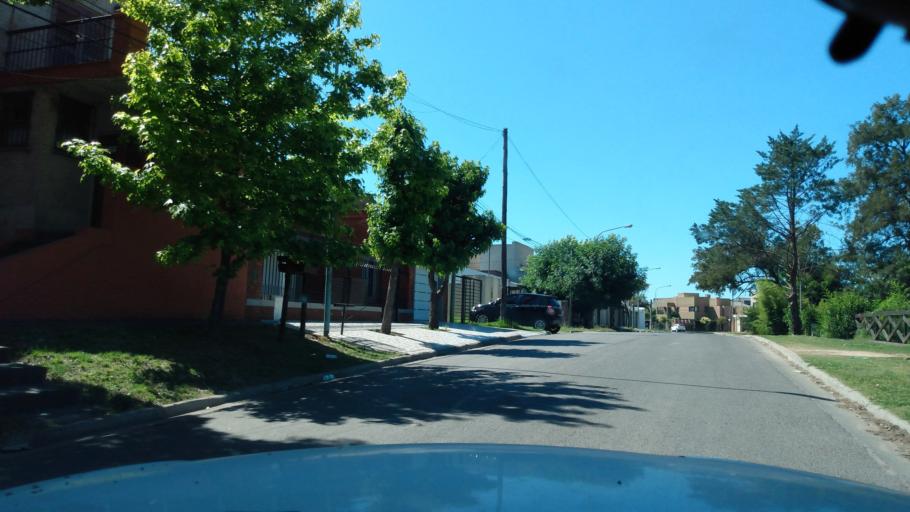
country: AR
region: Buenos Aires
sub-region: Partido de Lujan
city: Lujan
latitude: -34.5591
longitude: -59.1065
